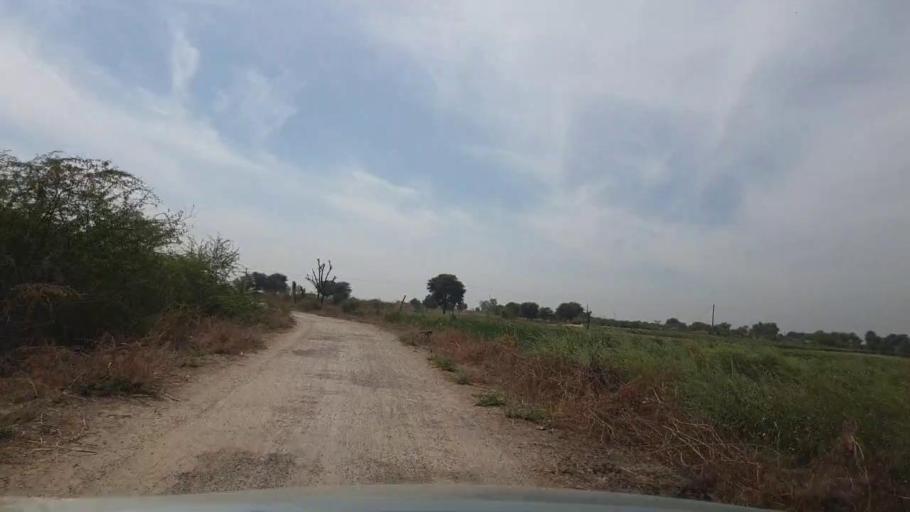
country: PK
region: Sindh
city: Nabisar
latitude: 25.1060
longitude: 69.6073
